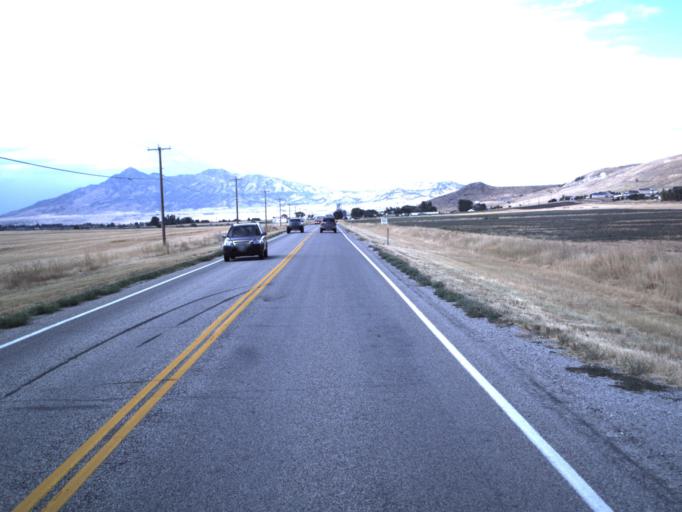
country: US
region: Utah
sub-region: Box Elder County
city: Garland
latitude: 41.7535
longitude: -112.0986
